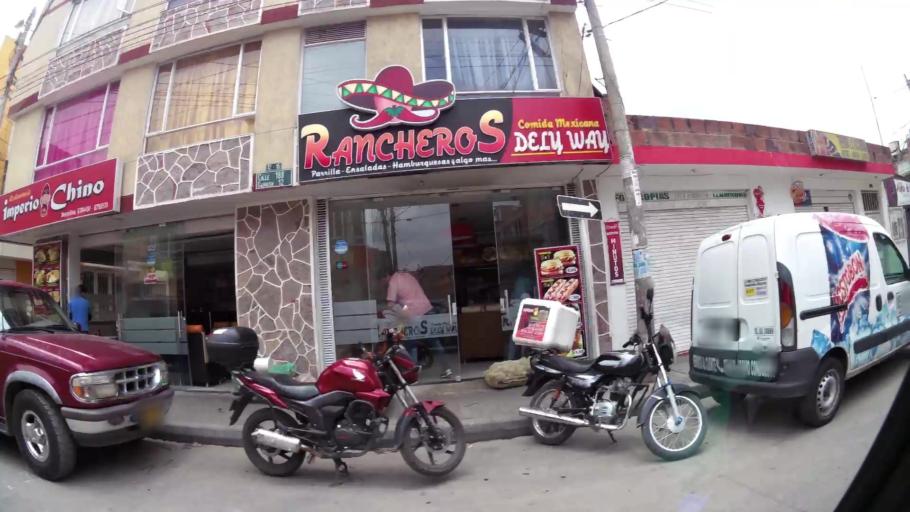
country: CO
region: Cundinamarca
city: La Calera
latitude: 4.7649
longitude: -74.0335
